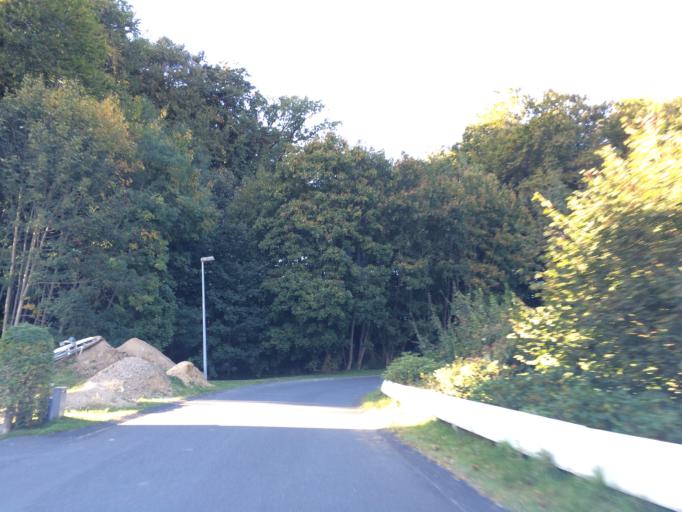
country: DK
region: Central Jutland
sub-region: Skanderborg Kommune
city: Ry
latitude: 56.1266
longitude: 9.7192
